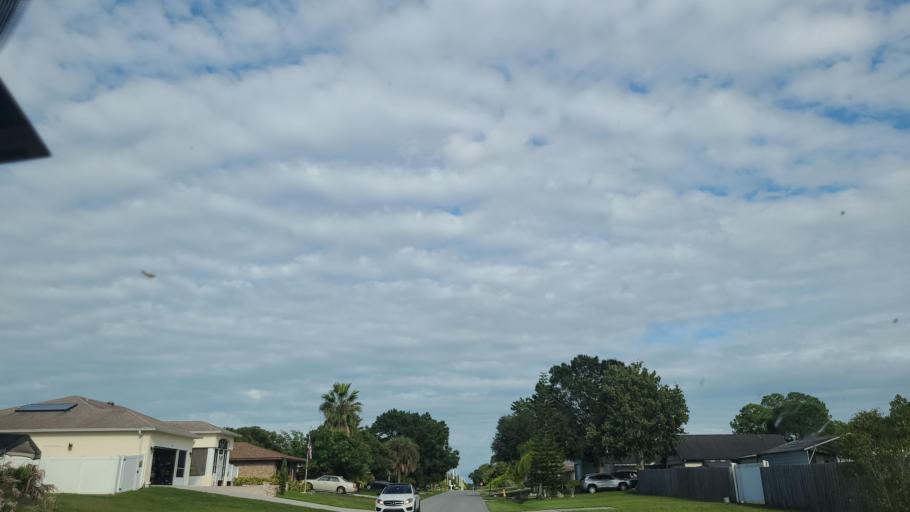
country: US
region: Florida
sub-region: Brevard County
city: Palm Bay
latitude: 27.9836
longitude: -80.6516
